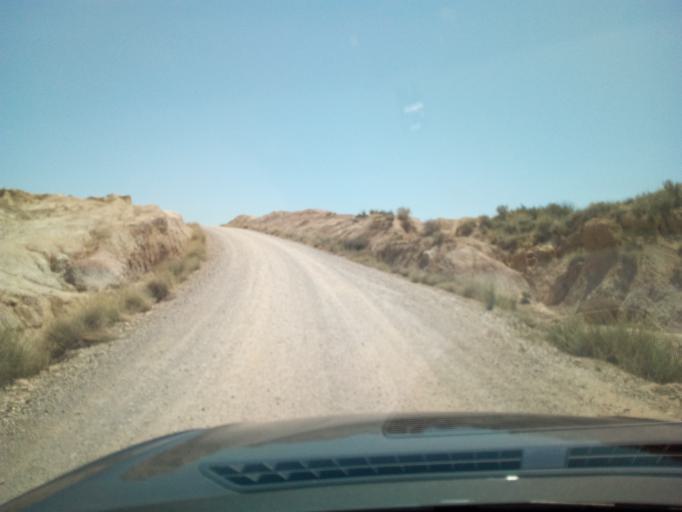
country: ES
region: Navarre
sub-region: Provincia de Navarra
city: Arguedas
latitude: 42.1828
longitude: -1.4746
